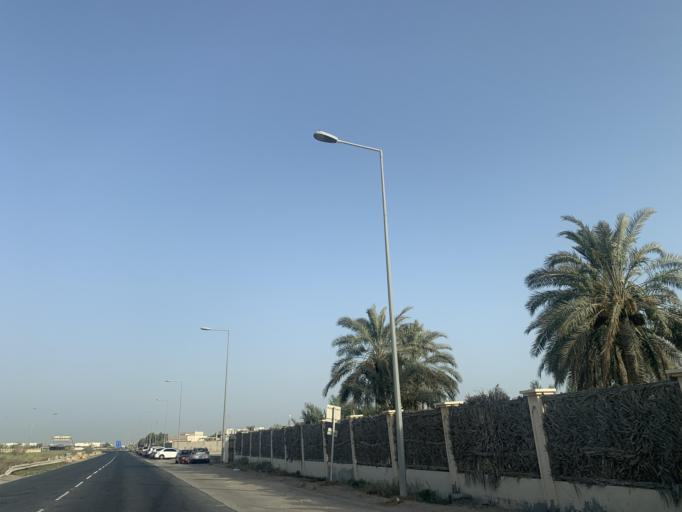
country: BH
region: Central Governorate
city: Madinat Hamad
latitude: 26.1748
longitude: 50.4596
